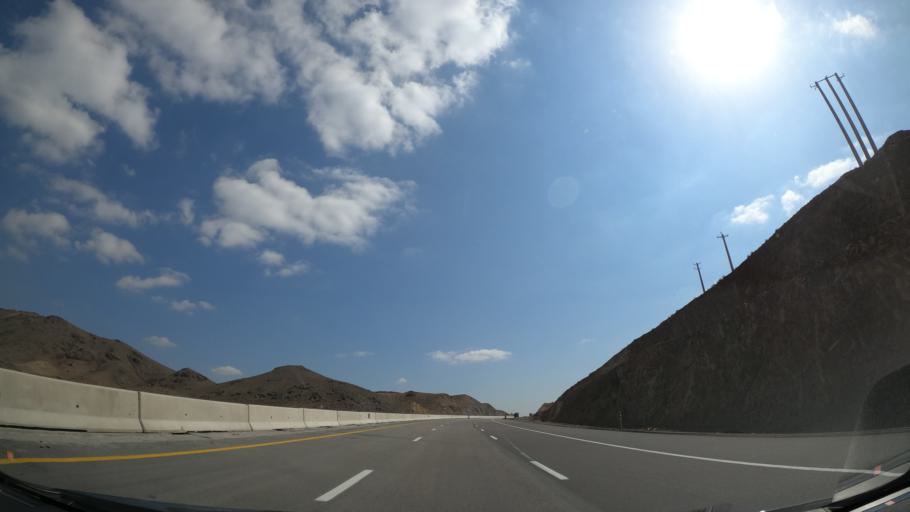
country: IR
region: Alborz
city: Nazarabad
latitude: 35.6830
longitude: 50.6409
